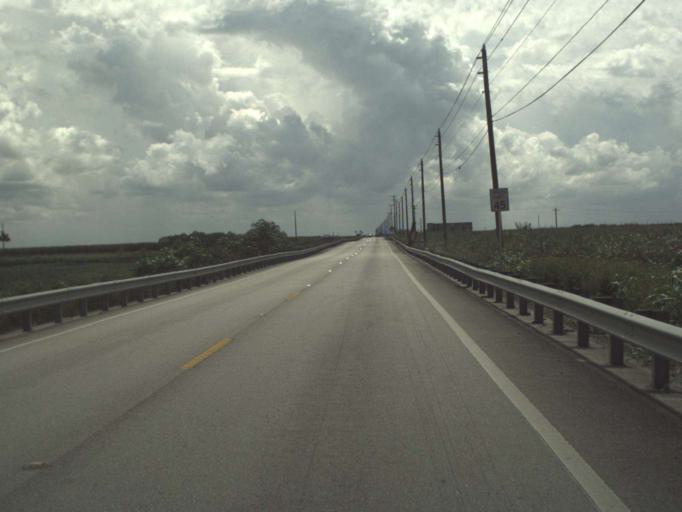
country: US
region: Florida
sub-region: Palm Beach County
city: Pahokee
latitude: 26.7874
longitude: -80.6534
